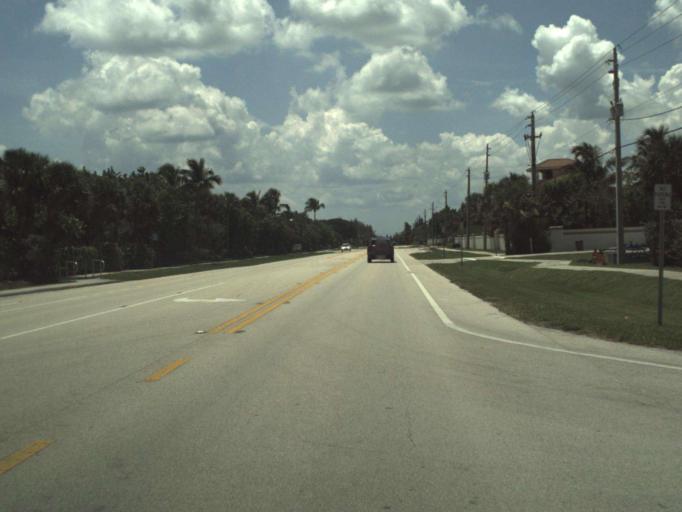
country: US
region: Florida
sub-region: Martin County
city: Sewall's Point
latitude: 27.2332
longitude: -80.1857
